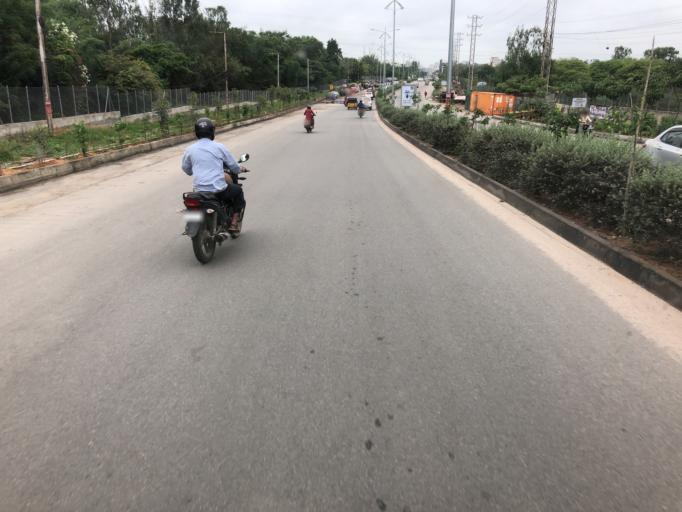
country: IN
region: Telangana
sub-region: Rangareddi
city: Kukatpalli
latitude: 17.4560
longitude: 78.3629
